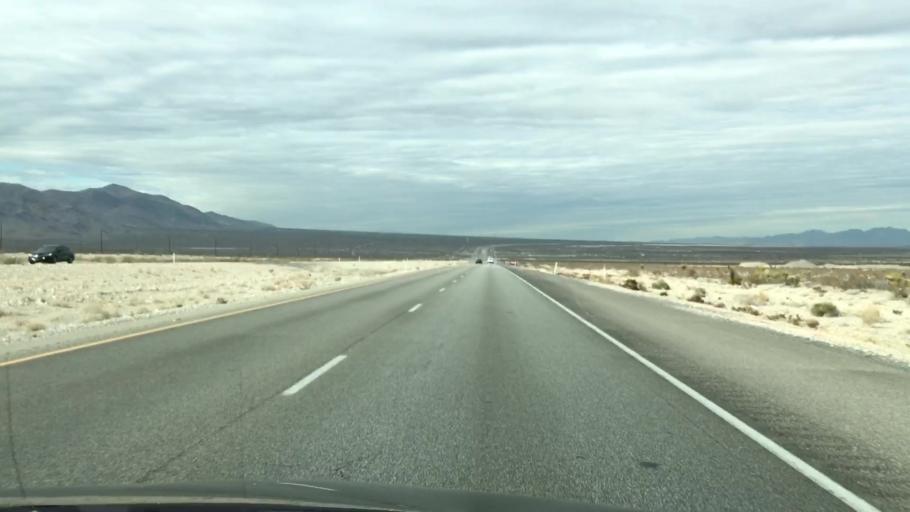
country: US
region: Nevada
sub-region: Clark County
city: Summerlin South
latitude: 36.3924
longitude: -115.3877
